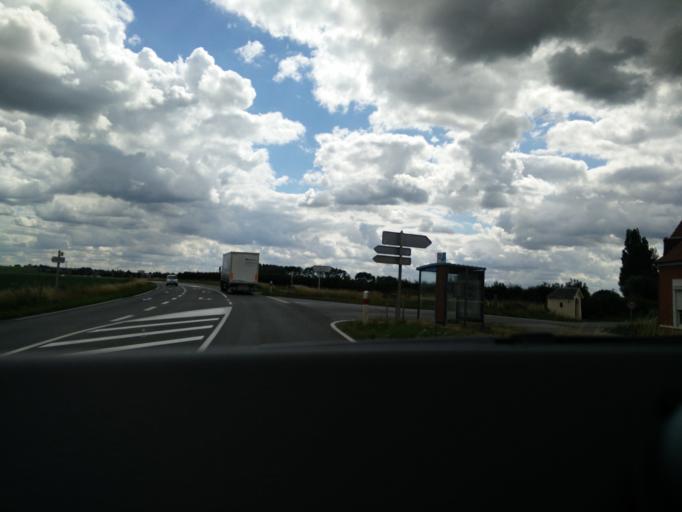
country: FR
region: Nord-Pas-de-Calais
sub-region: Departement du Nord
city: Steenvoorde
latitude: 50.7966
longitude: 2.5659
